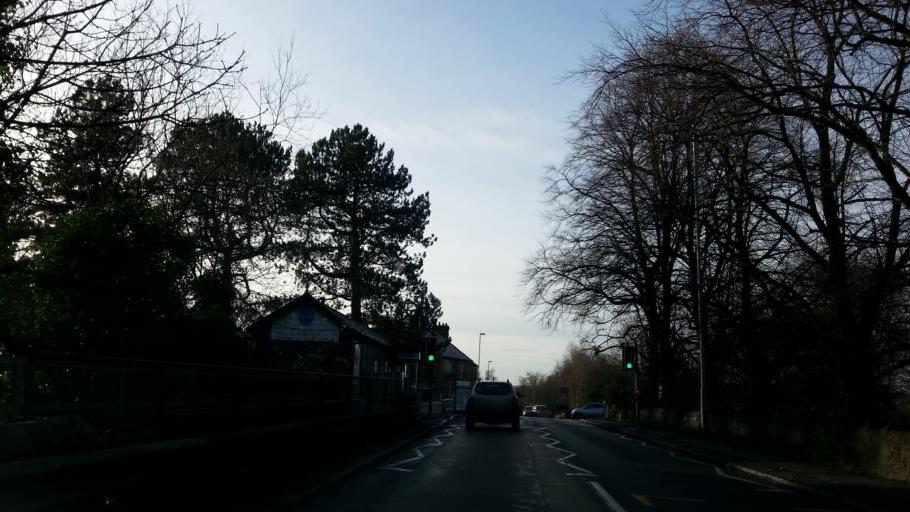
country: GB
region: England
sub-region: Staffordshire
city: Biddulph
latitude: 53.0659
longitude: -2.1240
